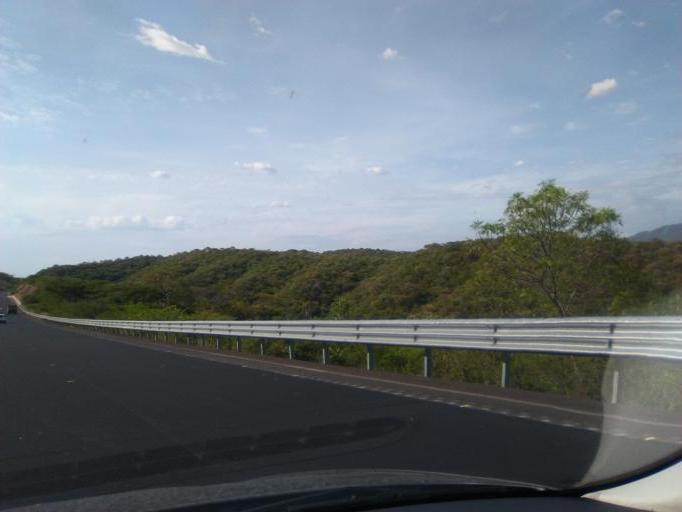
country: MX
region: Morelos
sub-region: Jojutla
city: Higueron
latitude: 18.4957
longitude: -99.1851
